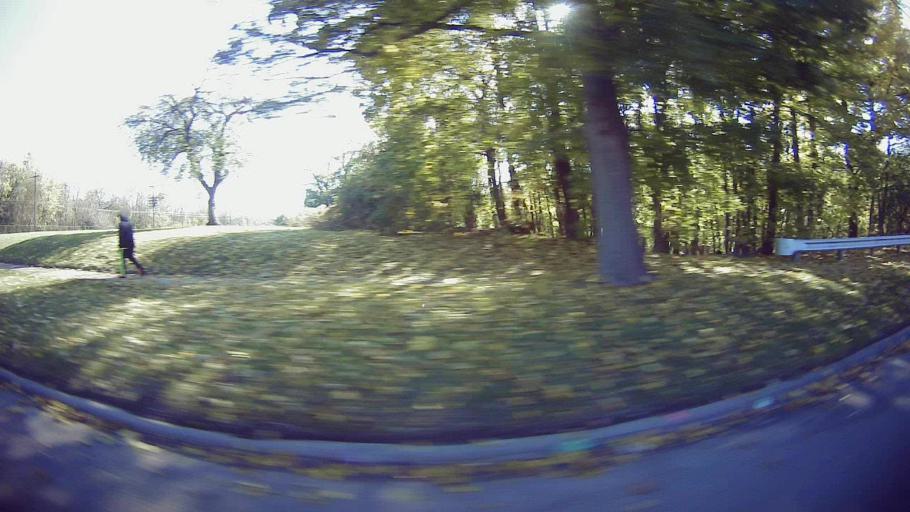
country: US
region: Michigan
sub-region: Wayne County
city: Redford
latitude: 42.4290
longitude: -83.2684
